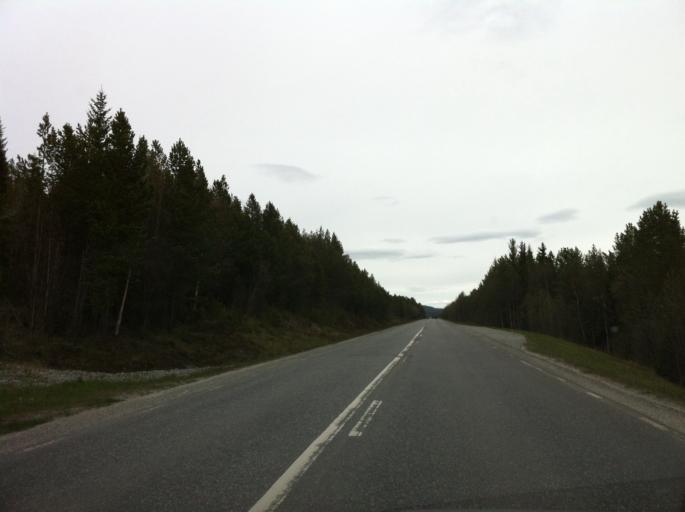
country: NO
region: Hedmark
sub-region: Engerdal
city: Engerdal
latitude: 62.5376
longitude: 12.5550
